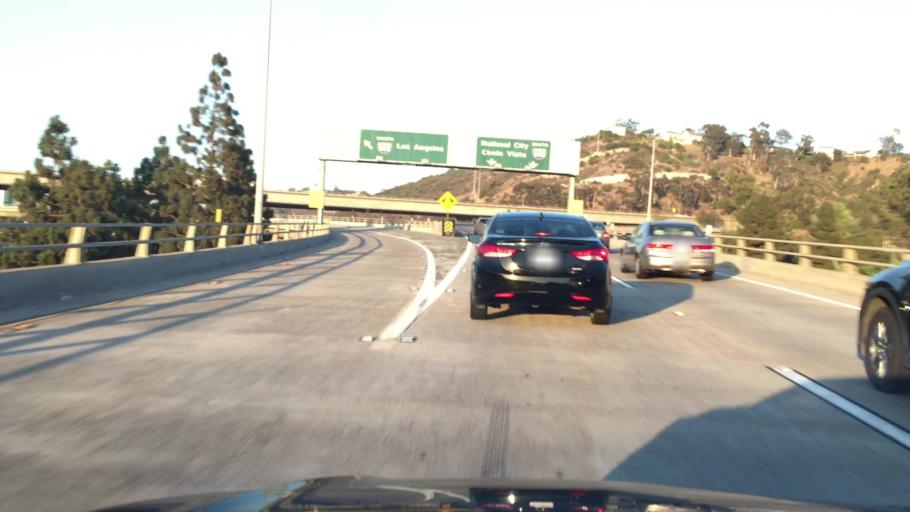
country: US
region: California
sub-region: San Diego County
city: San Diego
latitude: 32.7704
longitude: -117.1349
